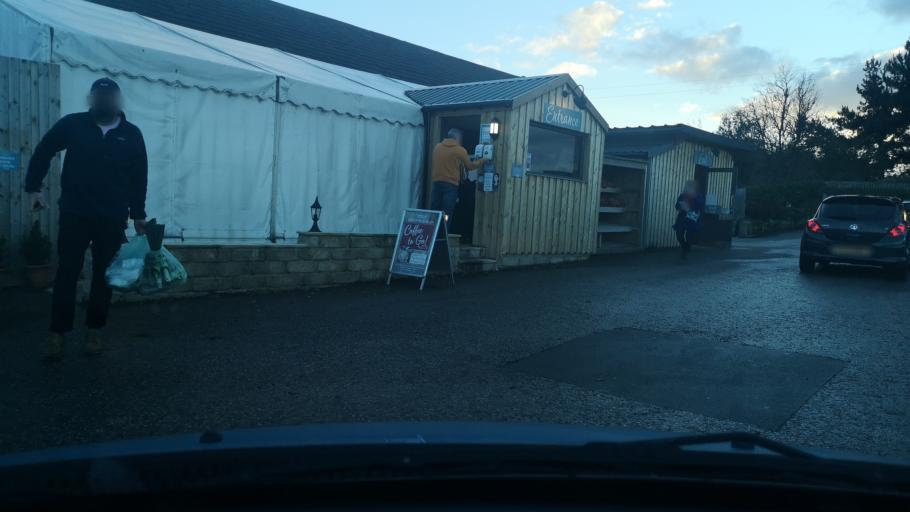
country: GB
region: England
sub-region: City and Borough of Wakefield
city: Crigglestone
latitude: 53.6383
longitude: -1.5469
